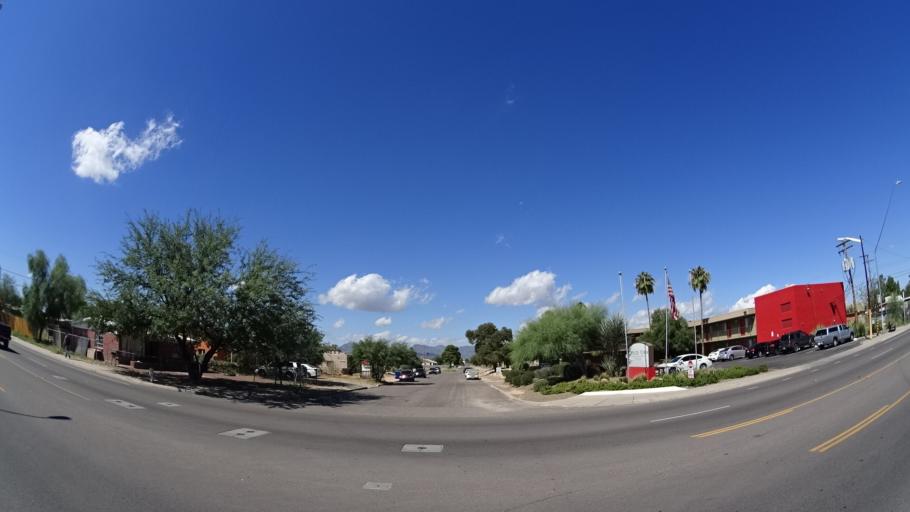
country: US
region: Arizona
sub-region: Pima County
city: Tucson
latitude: 32.2447
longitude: -110.9595
